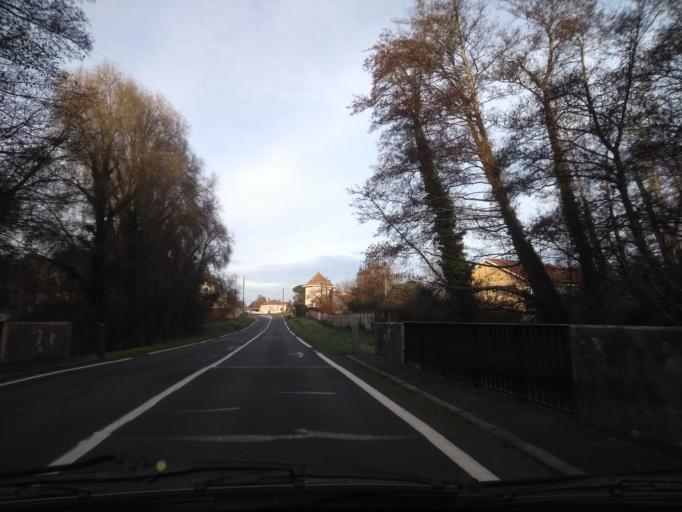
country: FR
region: Aquitaine
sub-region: Departement de la Gironde
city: Mios
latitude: 44.5996
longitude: -0.9163
